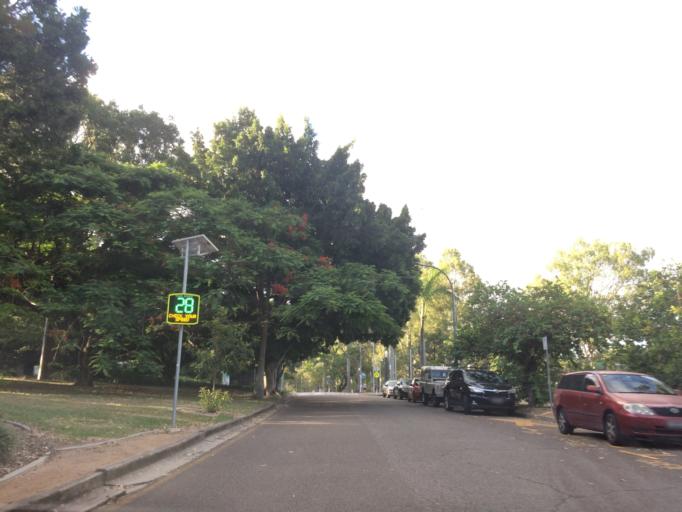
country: AU
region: Queensland
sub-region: Brisbane
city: South Brisbane
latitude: -27.4978
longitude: 153.0192
